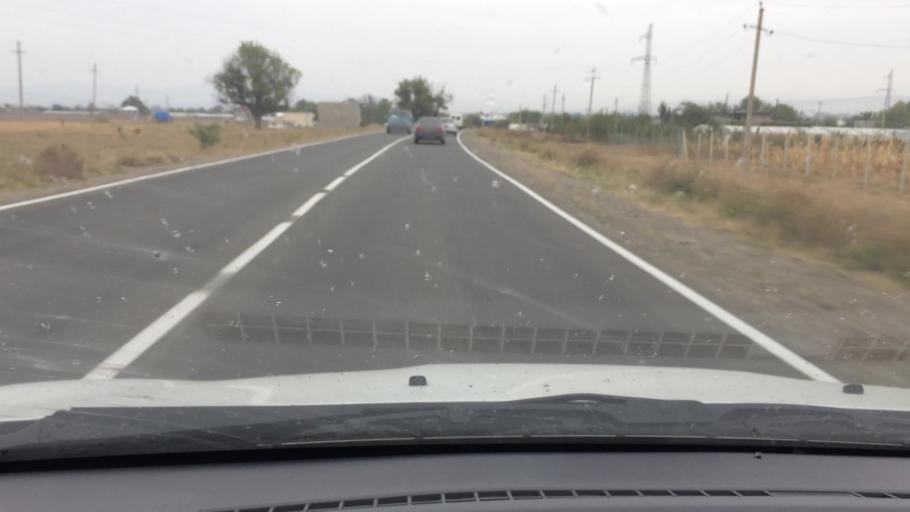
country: GE
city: Naghvarevi
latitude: 41.3919
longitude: 44.8280
